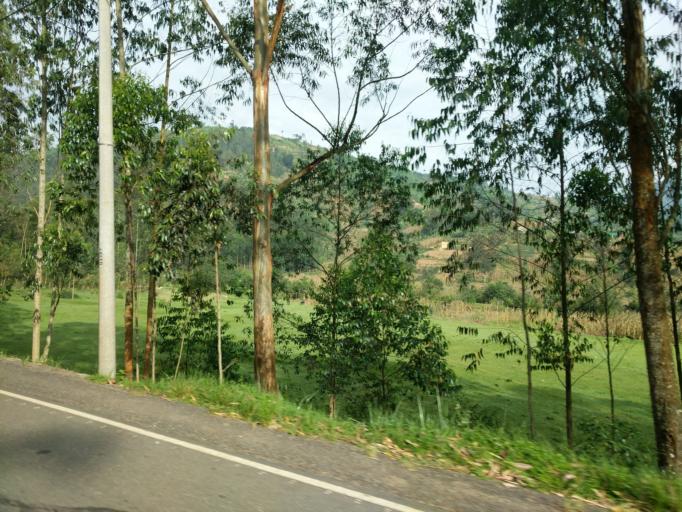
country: RW
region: Northern Province
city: Musanze
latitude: -1.6562
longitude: 29.8215
